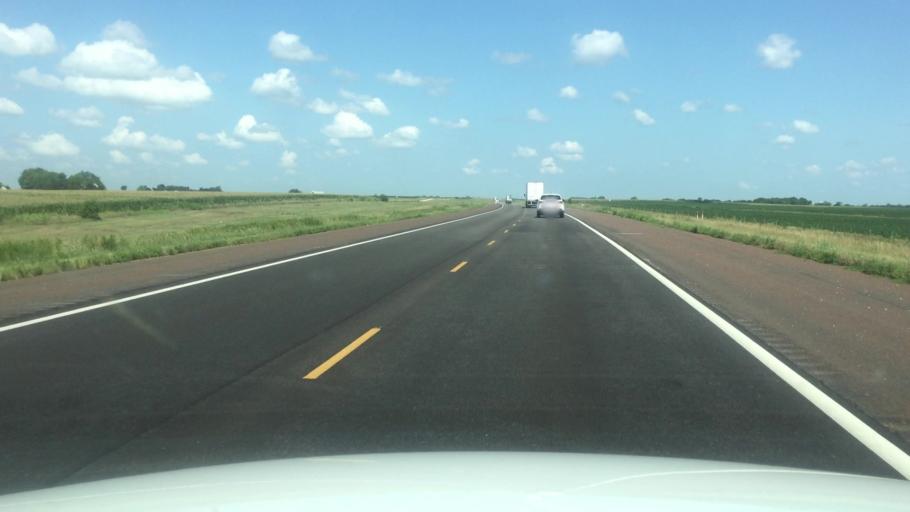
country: US
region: Kansas
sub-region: Nemaha County
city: Sabetha
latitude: 39.8501
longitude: -95.7459
